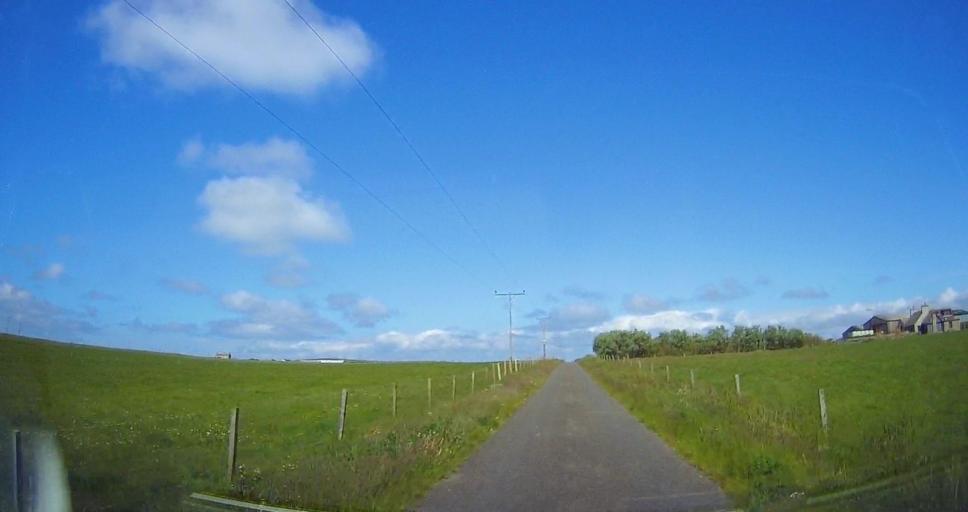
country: GB
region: Scotland
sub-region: Orkney Islands
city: Kirkwall
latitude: 58.8284
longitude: -2.8963
